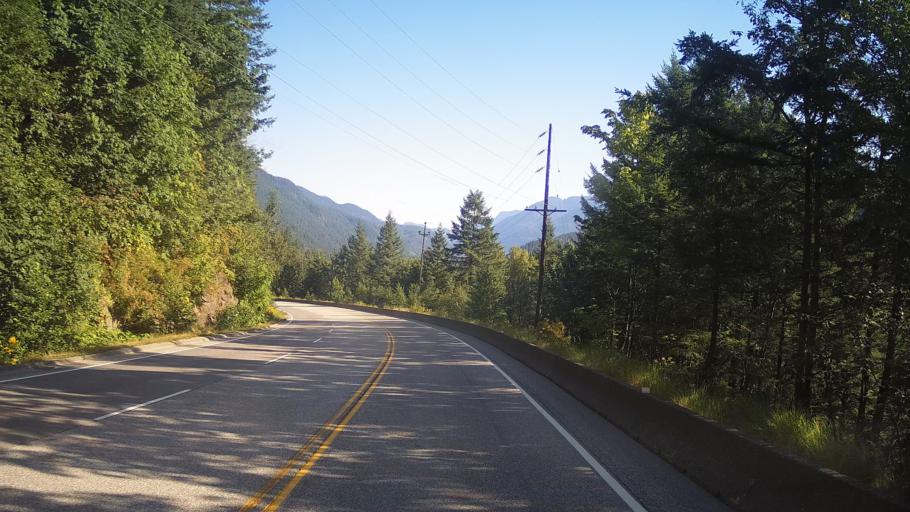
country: CA
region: British Columbia
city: Hope
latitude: 49.4192
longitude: -121.4367
